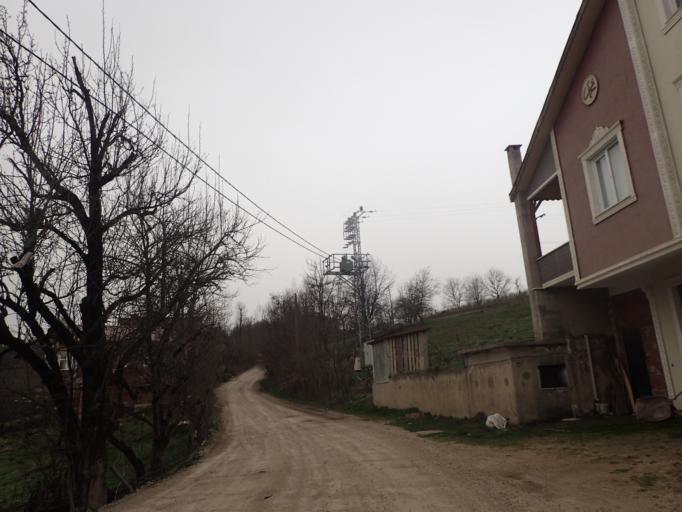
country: TR
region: Ordu
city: Kumru
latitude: 40.8247
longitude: 37.1875
